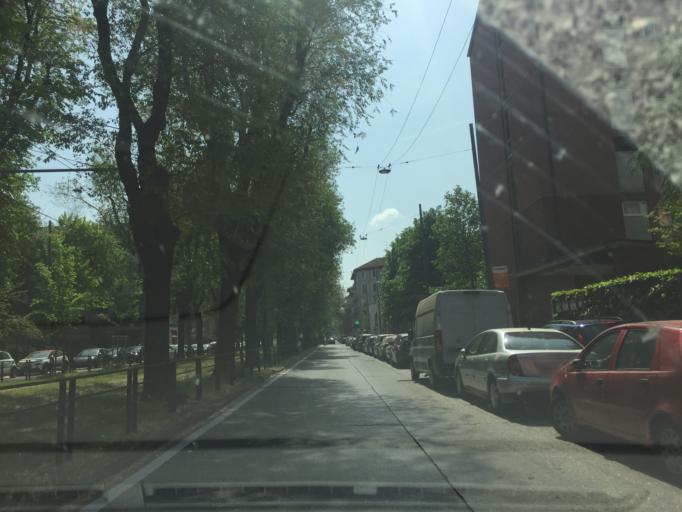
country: IT
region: Lombardy
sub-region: Citta metropolitana di Milano
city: Novate Milanese
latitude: 45.4986
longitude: 9.1517
